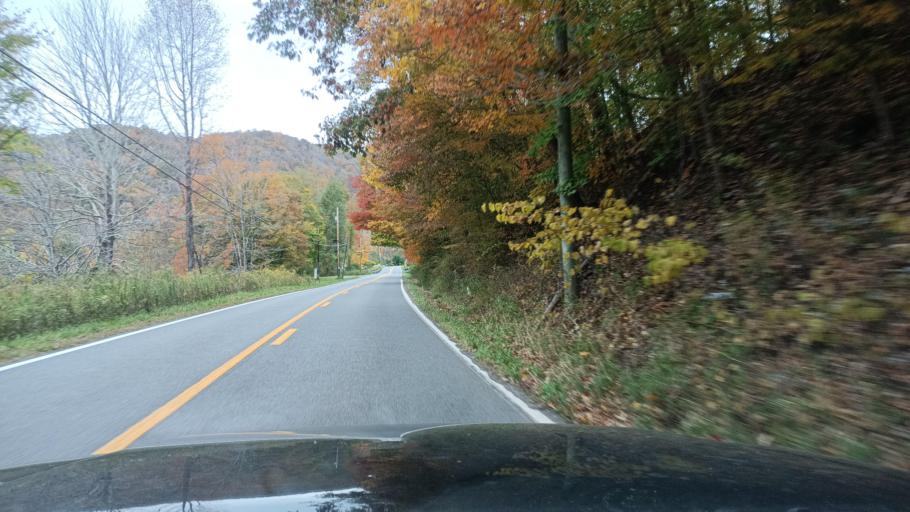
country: US
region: West Virginia
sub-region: Preston County
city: Kingwood
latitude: 39.3127
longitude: -79.6476
